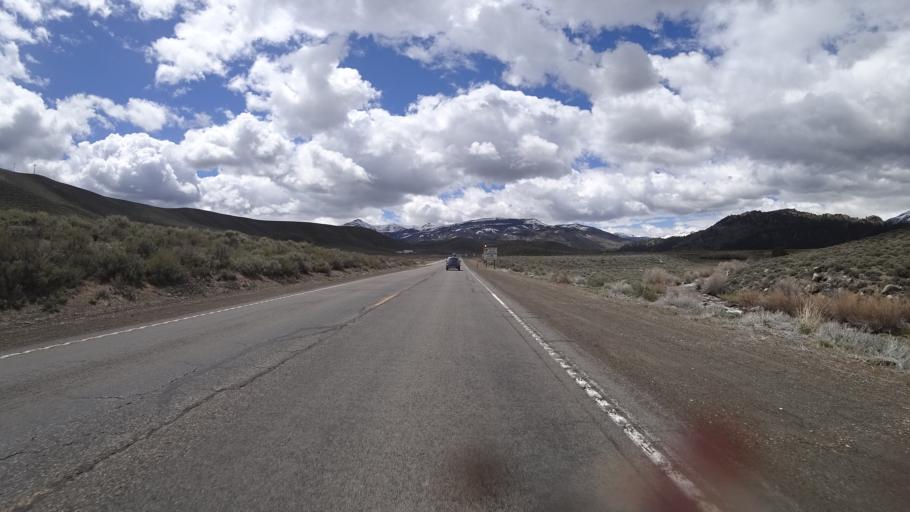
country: US
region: California
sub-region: Mono County
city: Bridgeport
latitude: 38.3575
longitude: -119.4448
